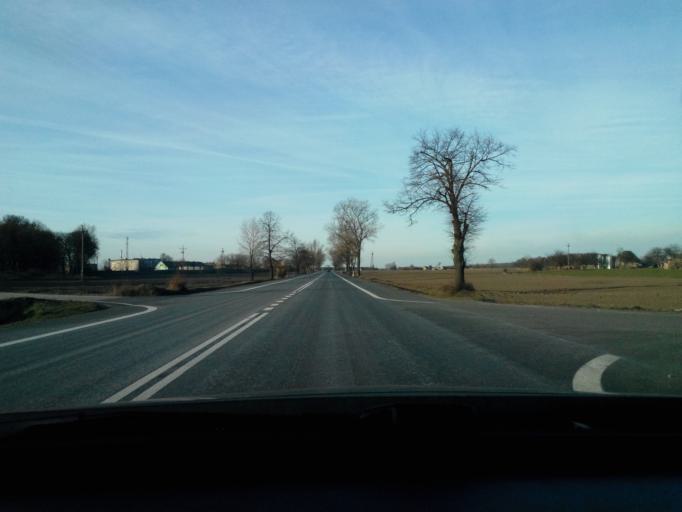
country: PL
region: Kujawsko-Pomorskie
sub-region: Powiat wloclawski
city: Lubien Kujawski
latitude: 52.3570
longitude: 19.1462
